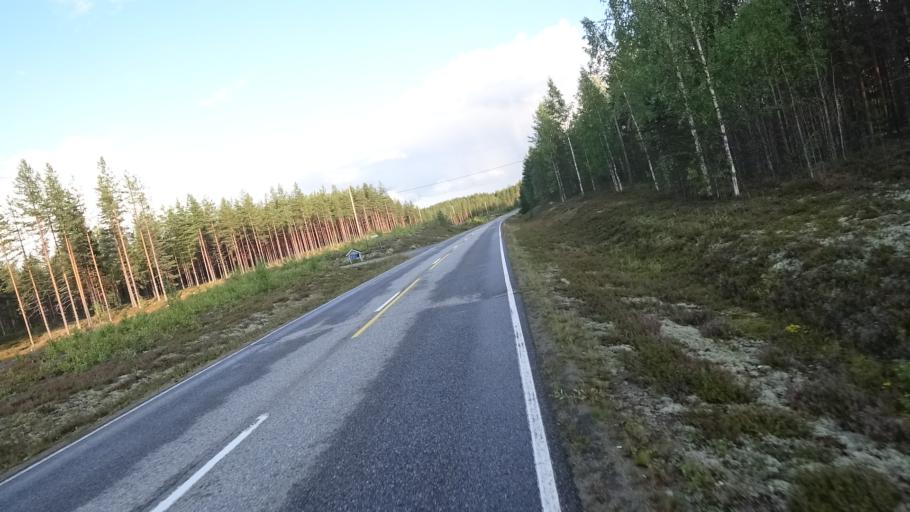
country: FI
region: North Karelia
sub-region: Joensuu
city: Ilomantsi
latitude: 62.6367
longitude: 31.0873
